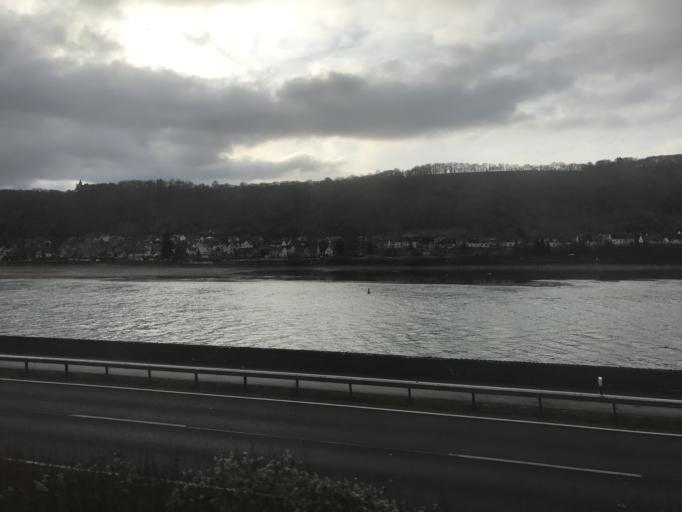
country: DE
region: Rheinland-Pfalz
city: Osterspai
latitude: 50.2510
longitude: 7.6099
